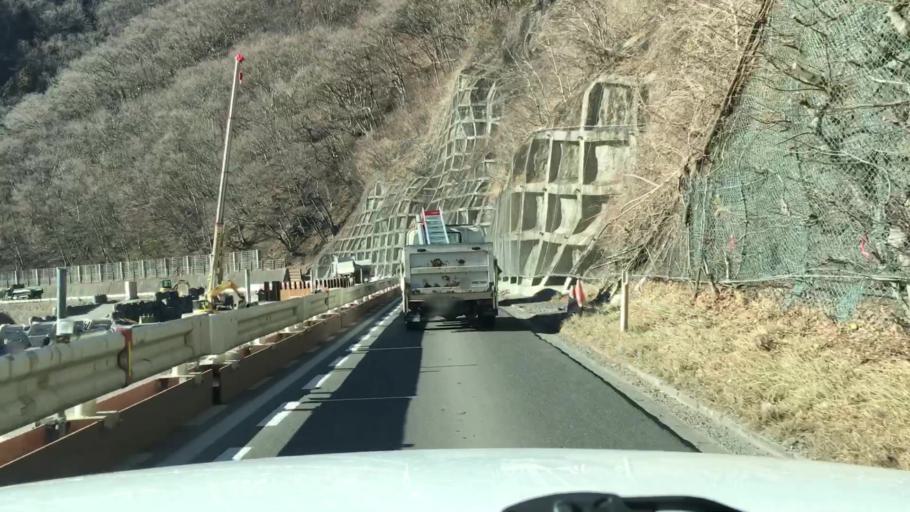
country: JP
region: Iwate
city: Miyako
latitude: 39.6281
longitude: 141.8122
